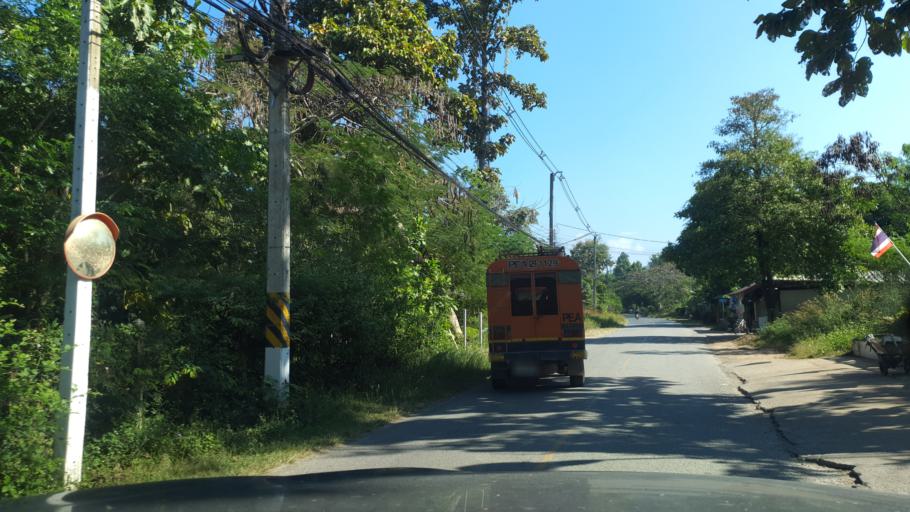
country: TH
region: Chiang Mai
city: San Sai
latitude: 18.8771
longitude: 99.1547
